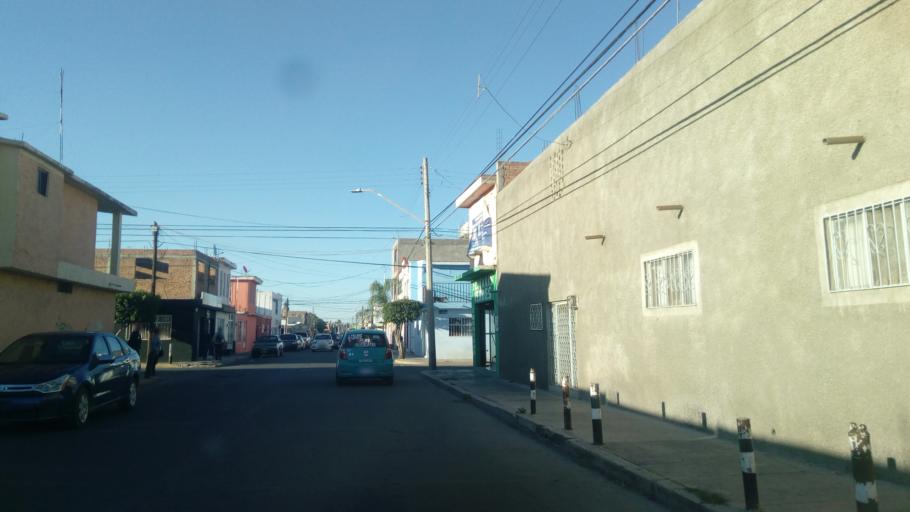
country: MX
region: Durango
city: Victoria de Durango
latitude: 24.0043
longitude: -104.6733
